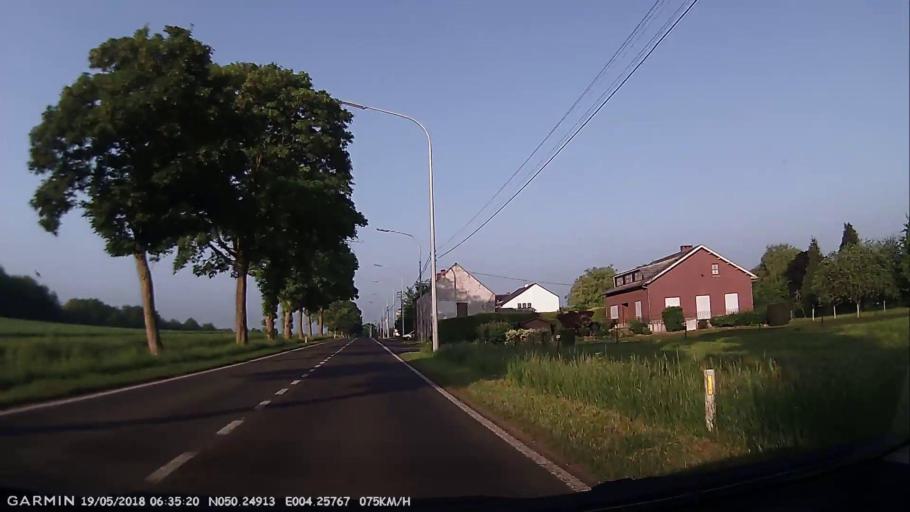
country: BE
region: Wallonia
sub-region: Province du Hainaut
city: Beaumont
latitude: 50.2490
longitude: 4.2575
